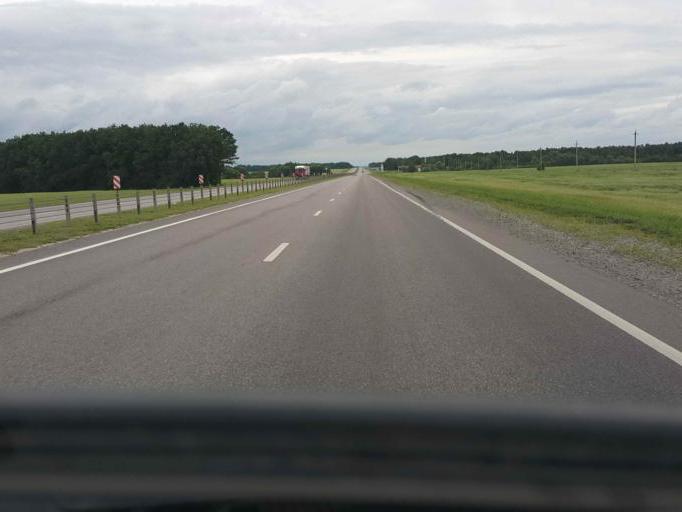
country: RU
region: Tambov
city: Zavoronezhskoye
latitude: 52.9039
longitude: 40.6495
